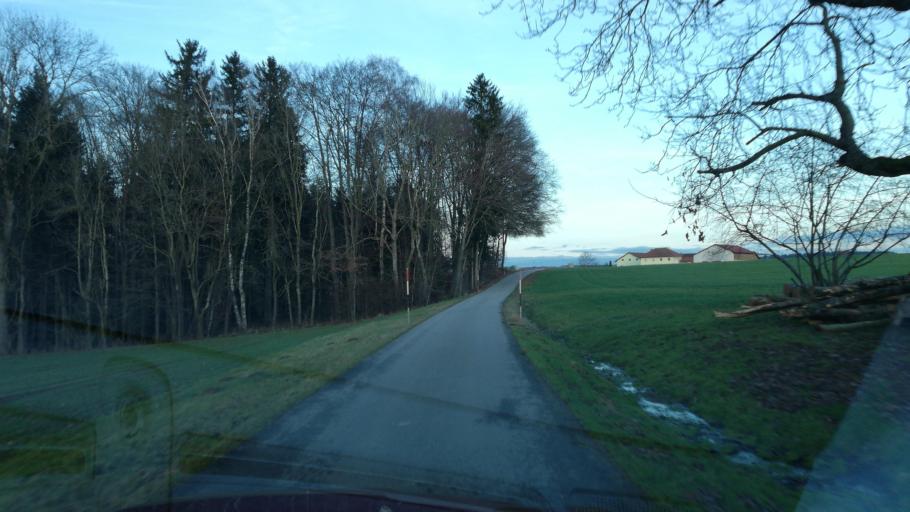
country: AT
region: Upper Austria
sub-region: Politischer Bezirk Braunau am Inn
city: Braunau am Inn
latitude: 48.1470
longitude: 13.0307
